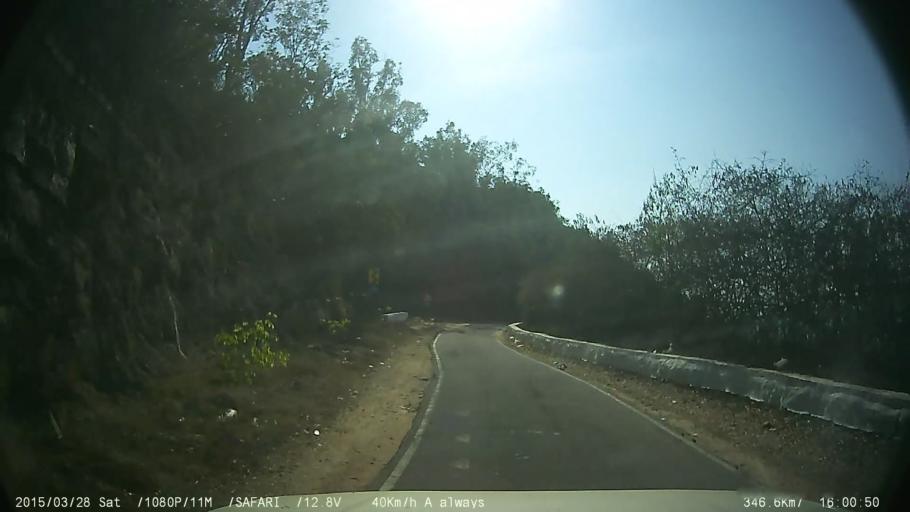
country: IN
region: Karnataka
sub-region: Mysore
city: Mysore
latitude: 12.2796
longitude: 76.6749
